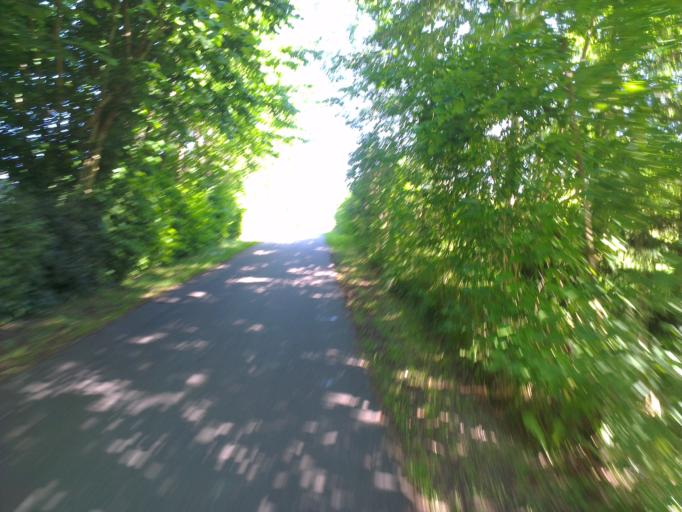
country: DK
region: Capital Region
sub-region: Halsnaes Kommune
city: Hundested
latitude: 55.9197
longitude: 11.9160
